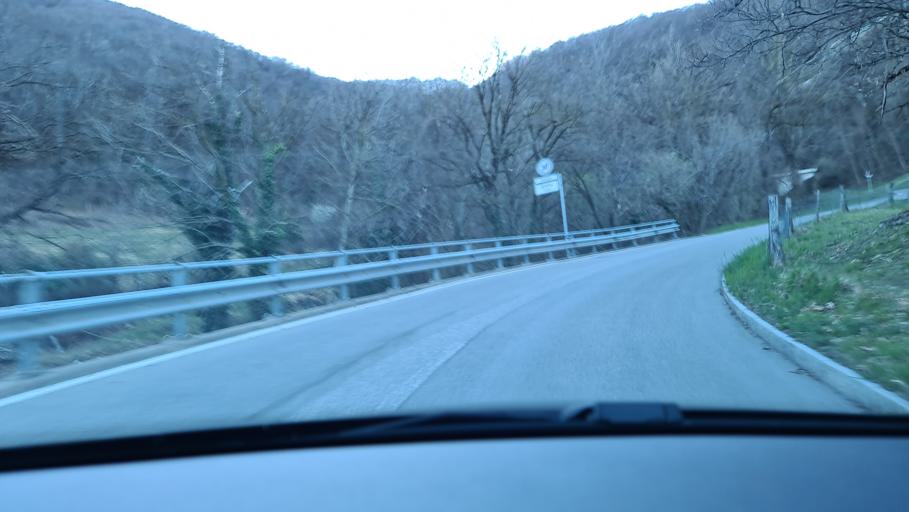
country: CH
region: Ticino
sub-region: Lugano District
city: Gravesano
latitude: 46.0394
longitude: 8.9140
